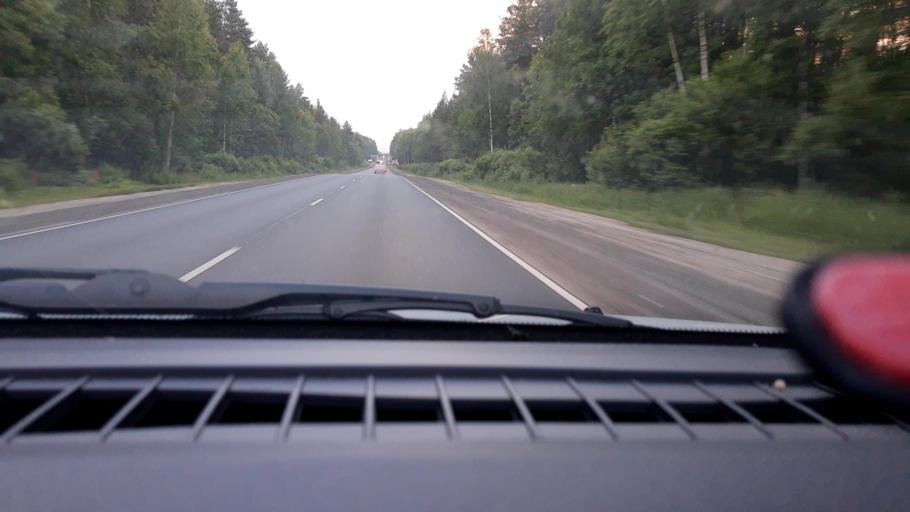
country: RU
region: Nizjnij Novgorod
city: Arzamas
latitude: 55.4249
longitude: 43.9068
